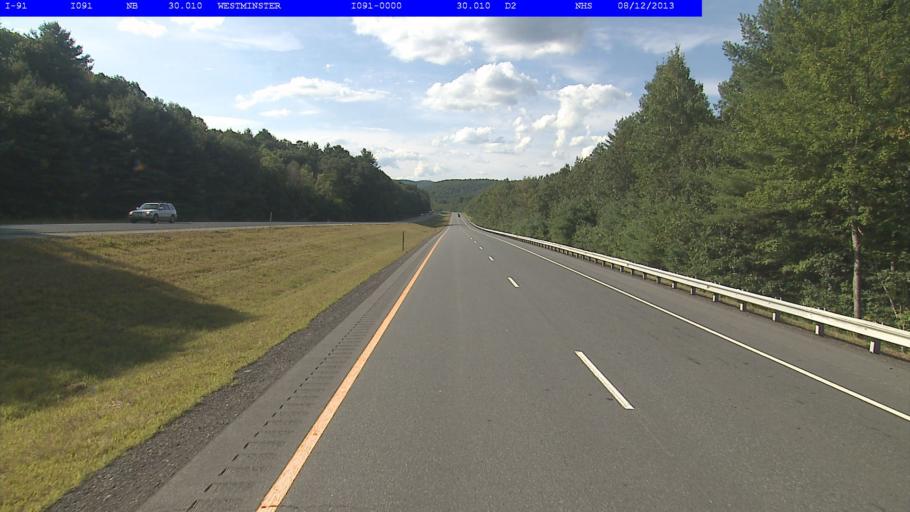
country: US
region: Vermont
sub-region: Windham County
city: Bellows Falls
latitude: 43.1109
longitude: -72.4572
